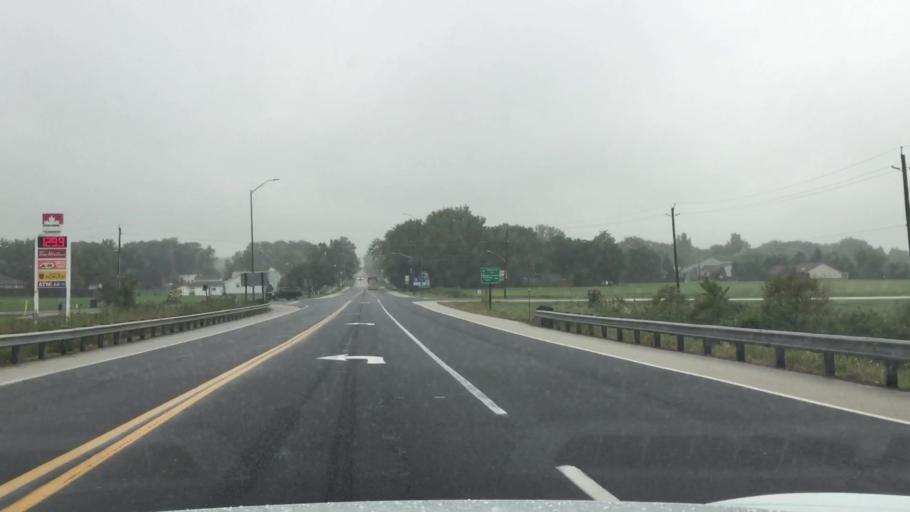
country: CA
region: Ontario
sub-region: Lambton County
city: Walpole Island
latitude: 42.2395
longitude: -82.5523
